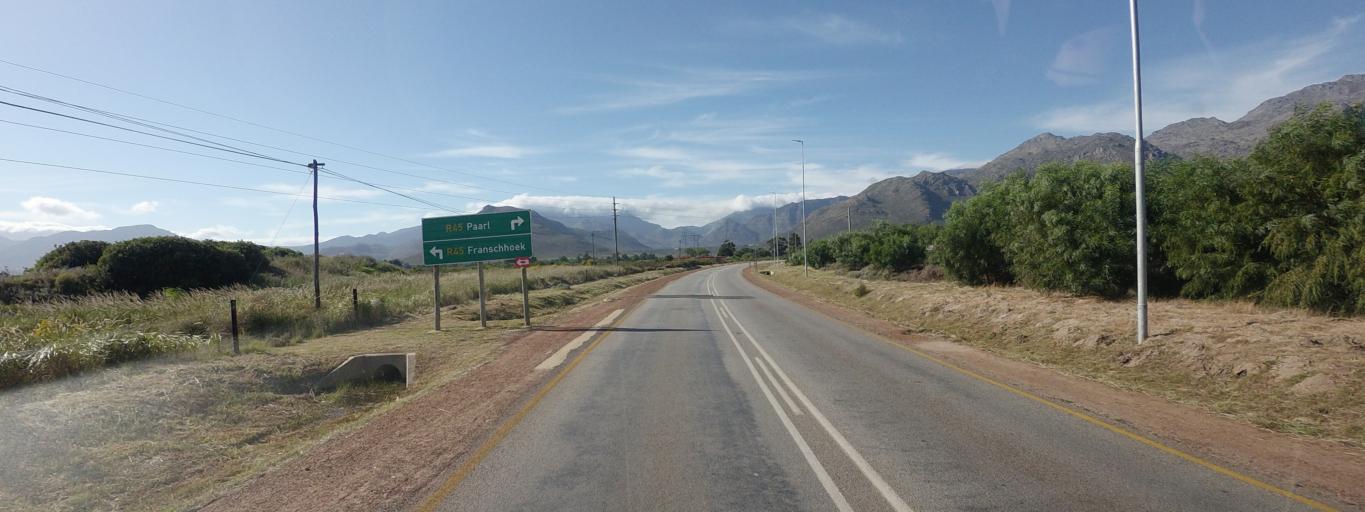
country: ZA
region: Western Cape
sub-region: Cape Winelands District Municipality
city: Paarl
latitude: -33.8726
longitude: 19.0443
